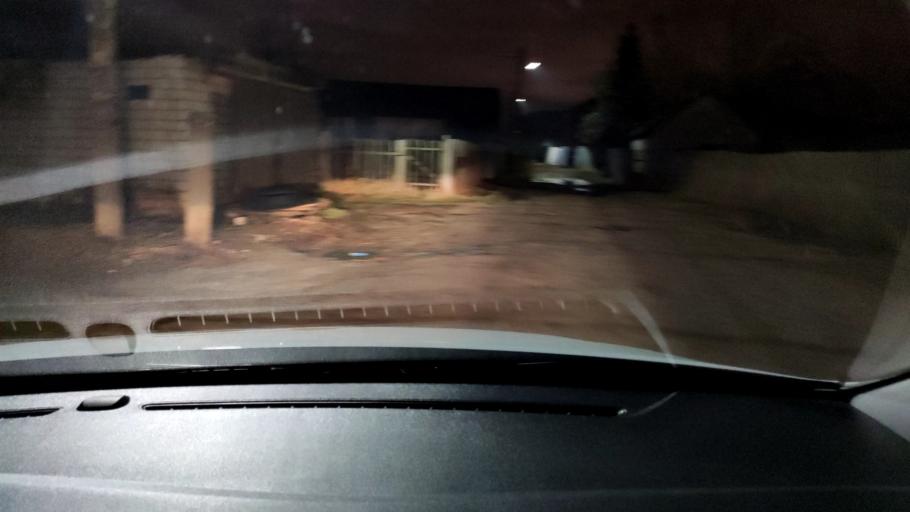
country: RU
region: Tatarstan
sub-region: Gorod Kazan'
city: Kazan
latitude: 55.8968
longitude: 49.1374
